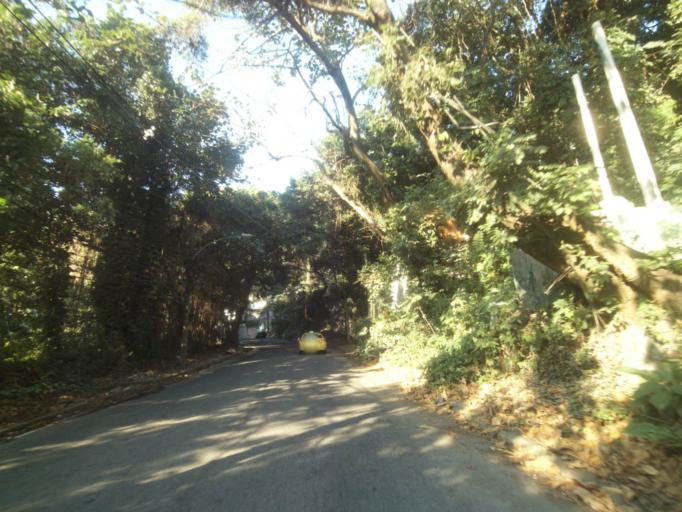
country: BR
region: Rio de Janeiro
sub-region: Rio De Janeiro
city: Rio de Janeiro
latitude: -23.0087
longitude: -43.2918
